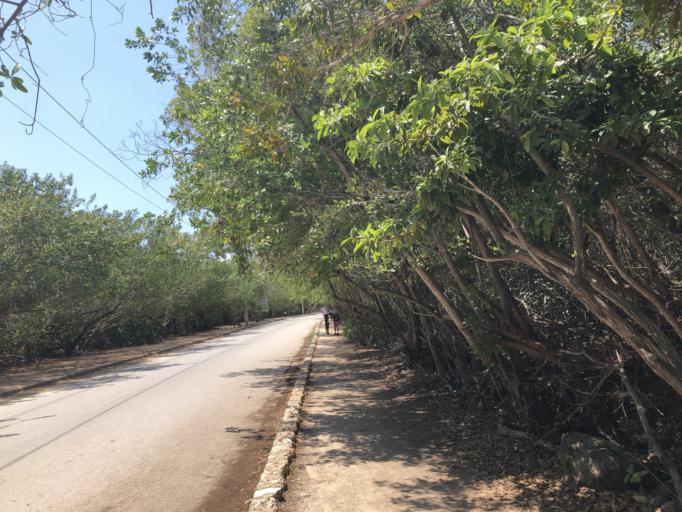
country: MX
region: Quintana Roo
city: Tulum
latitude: 20.2156
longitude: -87.4326
